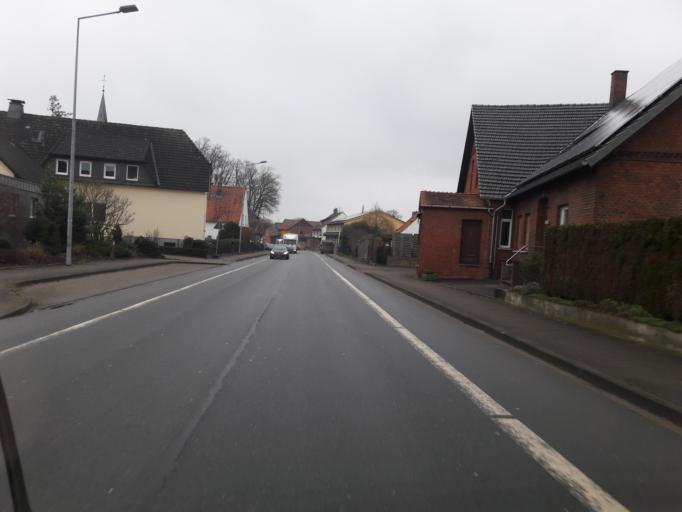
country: DE
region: North Rhine-Westphalia
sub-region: Regierungsbezirk Detmold
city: Hille
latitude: 52.3126
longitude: 8.8254
